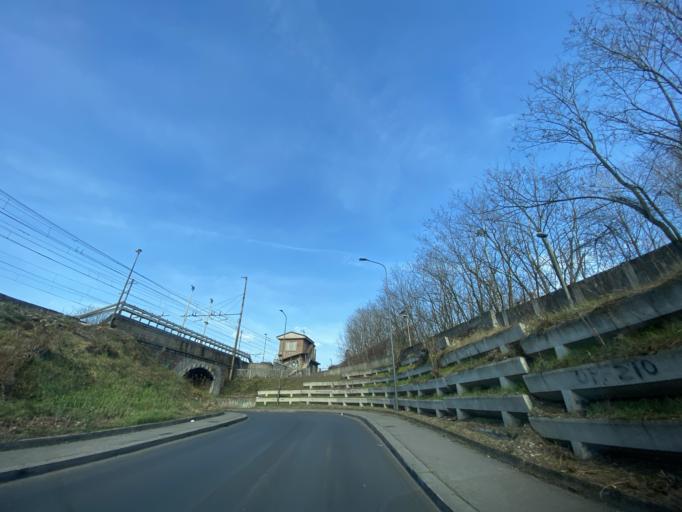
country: IT
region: Lombardy
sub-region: Citta metropolitana di Milano
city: Novate Milanese
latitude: 45.5081
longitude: 9.1489
